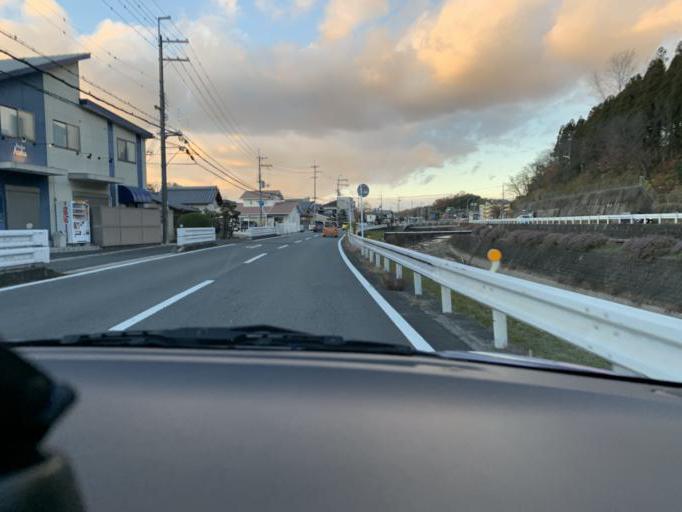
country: JP
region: Nara
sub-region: Ikoma-shi
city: Ikoma
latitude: 34.7147
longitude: 135.7240
